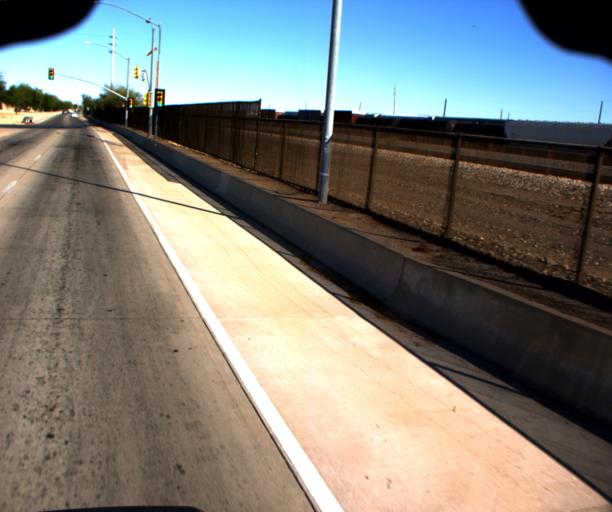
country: US
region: Arizona
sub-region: Pima County
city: Tucson
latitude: 32.1982
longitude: -110.9279
